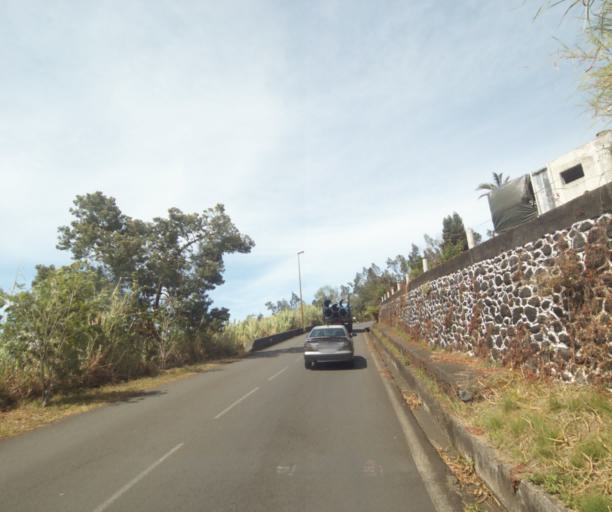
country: RE
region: Reunion
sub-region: Reunion
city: Saint-Paul
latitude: -21.0401
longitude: 55.3183
